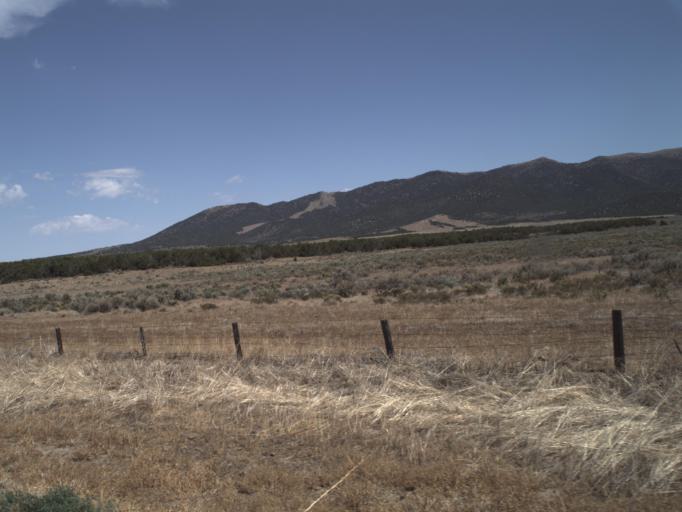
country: US
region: Utah
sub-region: Utah County
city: Genola
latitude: 39.9387
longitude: -112.1824
